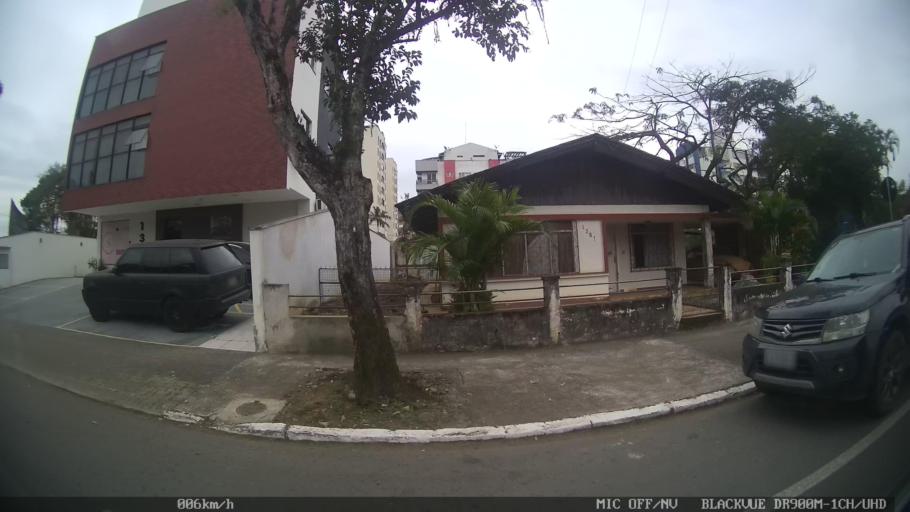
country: BR
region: Santa Catarina
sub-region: Joinville
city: Joinville
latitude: -26.2846
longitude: -48.8450
